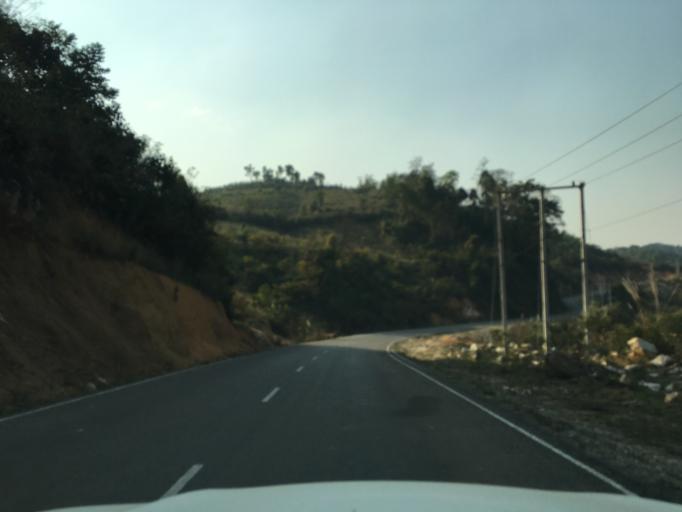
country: LA
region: Houaphan
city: Xam Nua
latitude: 20.5705
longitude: 104.0584
